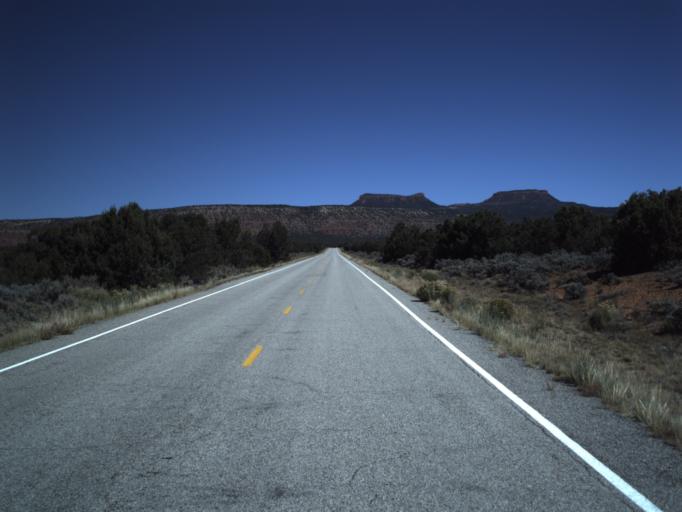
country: US
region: Utah
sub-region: San Juan County
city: Blanding
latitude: 37.5625
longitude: -109.9297
